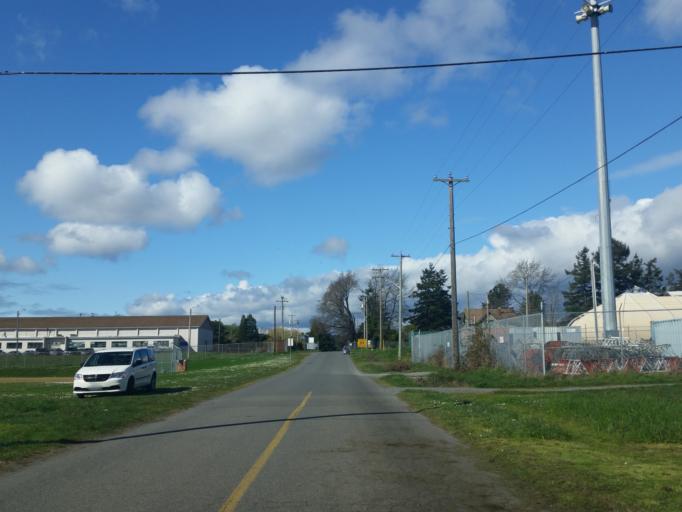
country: CA
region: British Columbia
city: Victoria
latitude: 48.4211
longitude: -123.4053
